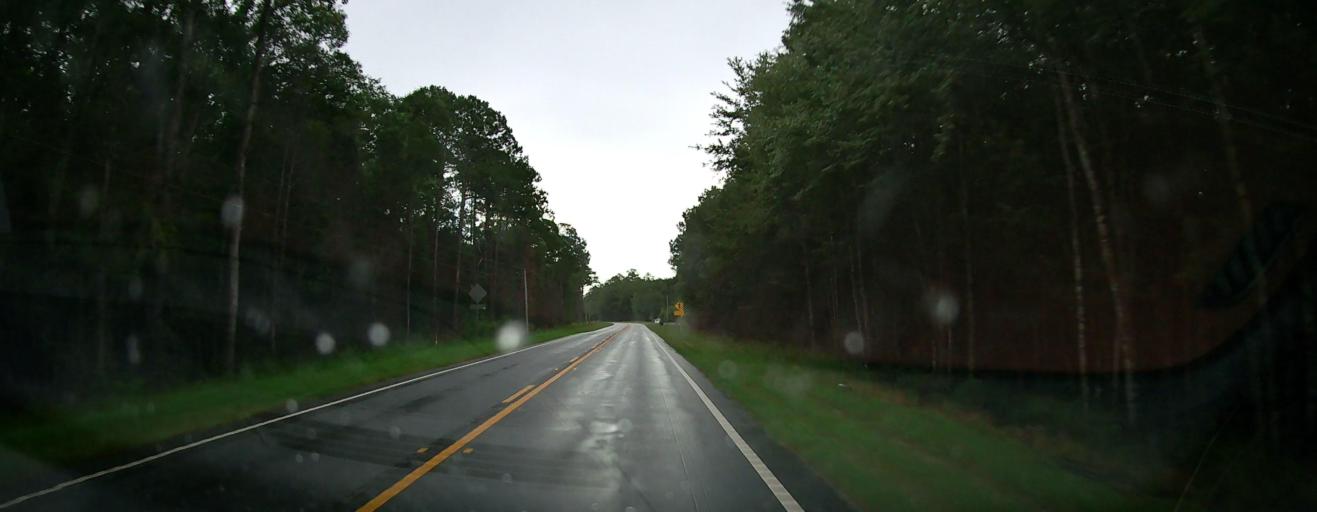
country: US
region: Georgia
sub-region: Glynn County
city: Dock Junction
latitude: 31.3177
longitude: -81.7479
